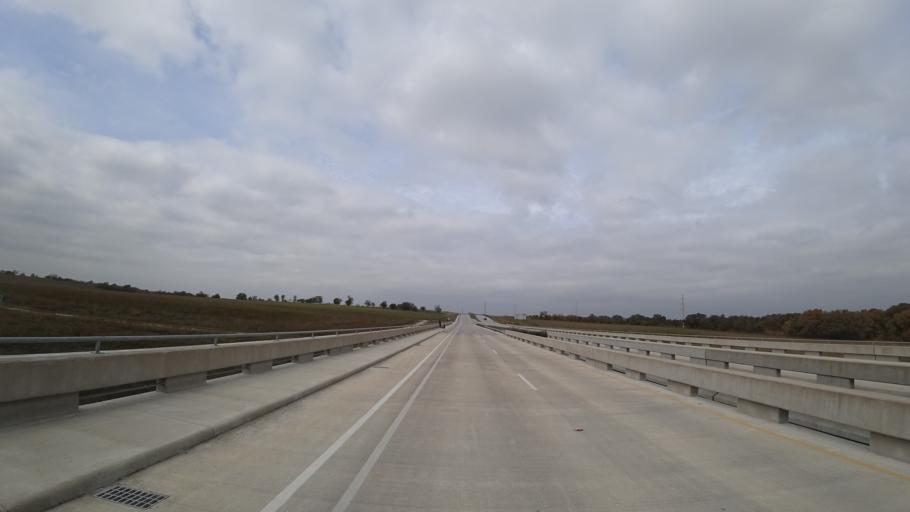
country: US
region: Texas
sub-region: Travis County
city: Manor
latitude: 30.3713
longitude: -97.5899
